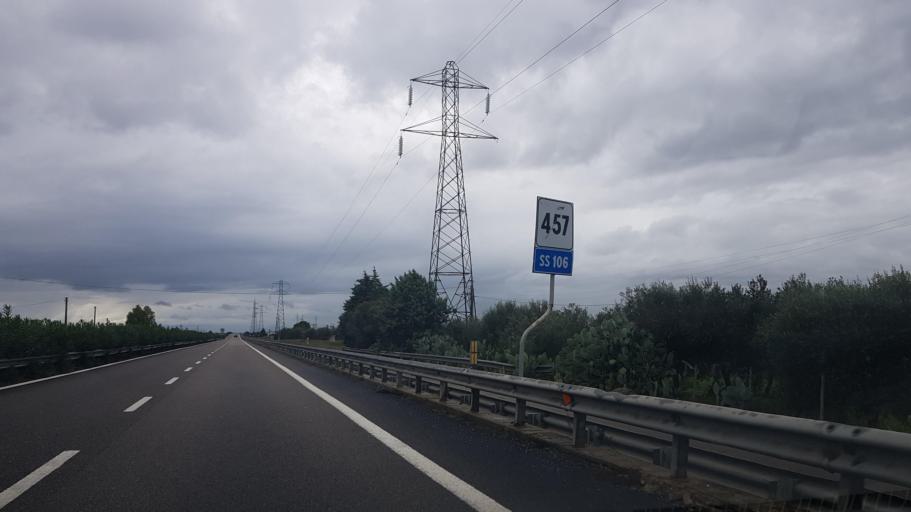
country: IT
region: Apulia
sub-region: Provincia di Taranto
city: Marina di Ginosa
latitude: 40.4478
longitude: 16.8570
